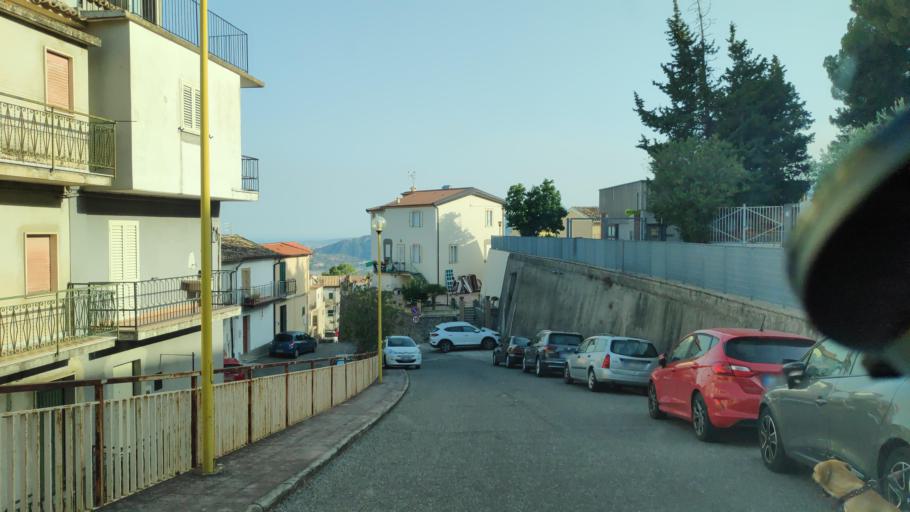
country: IT
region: Calabria
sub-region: Provincia di Catanzaro
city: Sant'Andrea Apostolo dello Ionio
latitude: 38.6200
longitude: 16.5318
